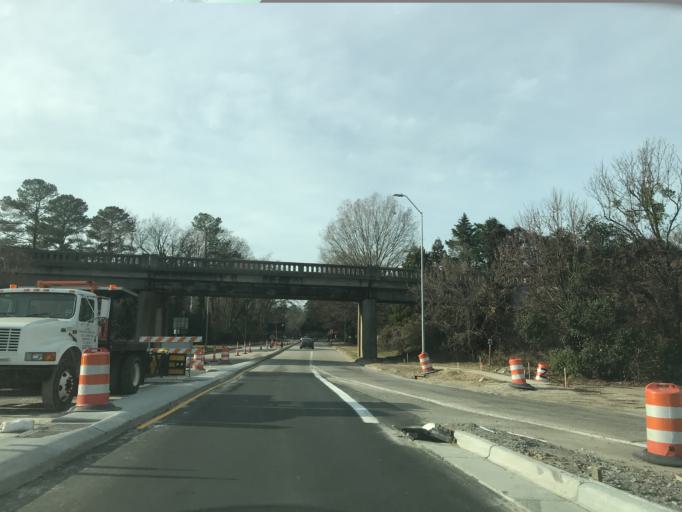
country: US
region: North Carolina
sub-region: Wake County
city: West Raleigh
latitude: 35.7965
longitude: -78.6420
